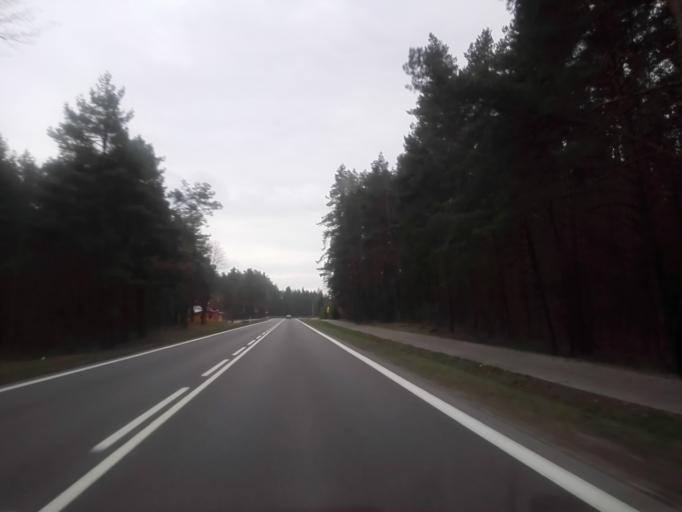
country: PL
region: Podlasie
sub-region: Powiat grajewski
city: Rajgrod
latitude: 53.7104
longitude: 22.6714
